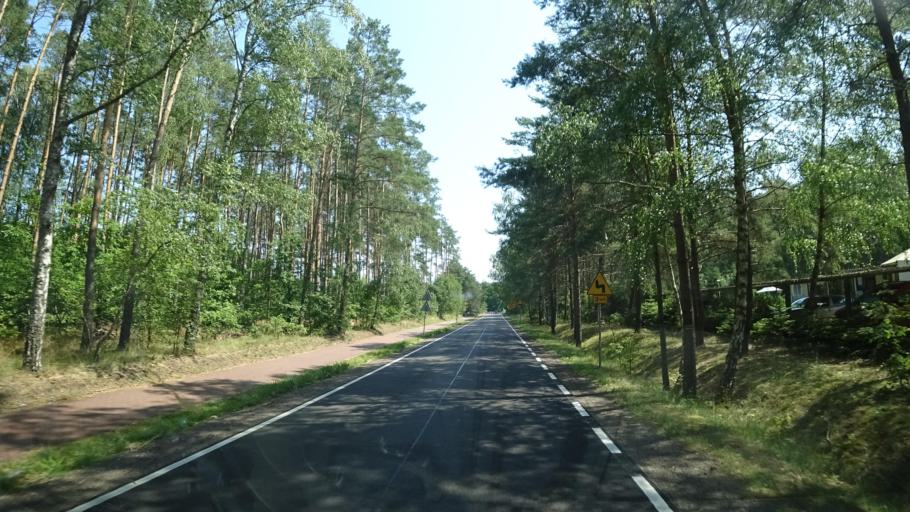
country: PL
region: Pomeranian Voivodeship
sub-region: Powiat chojnicki
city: Brusy
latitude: 53.8517
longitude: 17.5719
